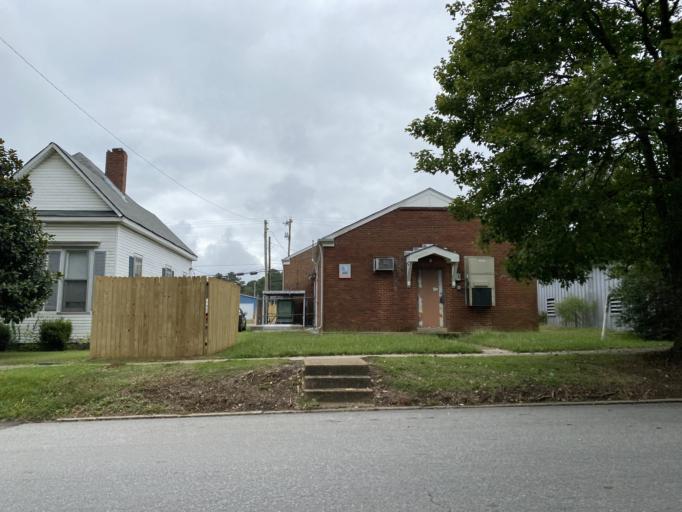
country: US
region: Alabama
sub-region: Franklin County
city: Red Bay
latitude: 34.4424
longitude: -88.1468
